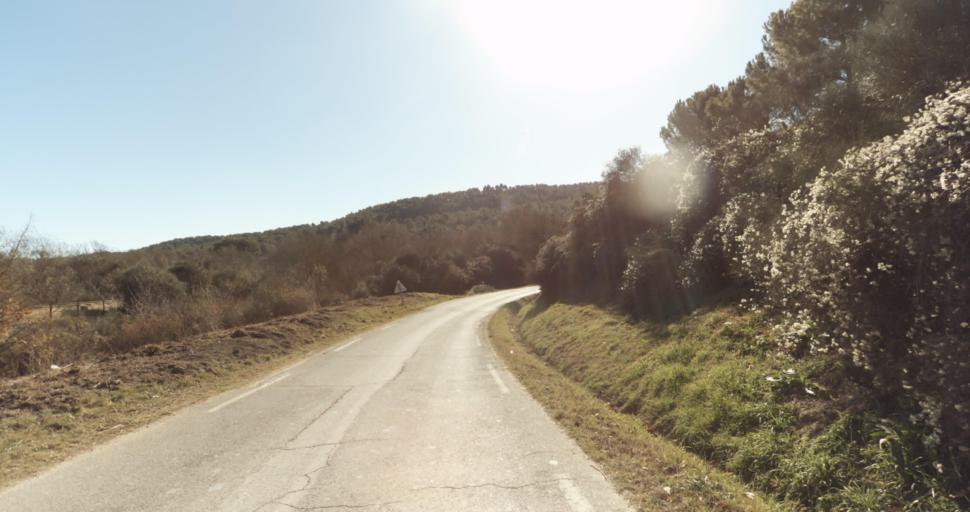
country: FR
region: Provence-Alpes-Cote d'Azur
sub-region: Departement des Bouches-du-Rhone
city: Peypin
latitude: 43.3962
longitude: 5.5652
